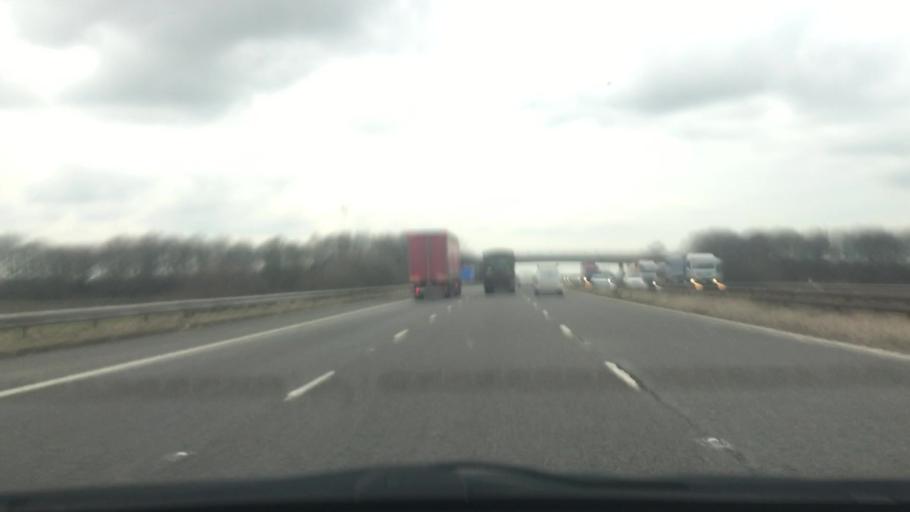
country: GB
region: England
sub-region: Doncaster
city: Hatfield
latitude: 53.5802
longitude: -0.9420
